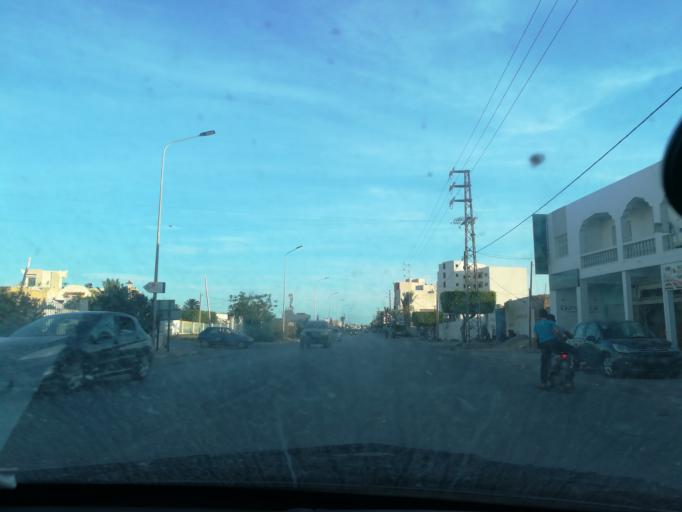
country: TN
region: Safaqis
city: Al Qarmadah
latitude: 34.8111
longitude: 10.7616
